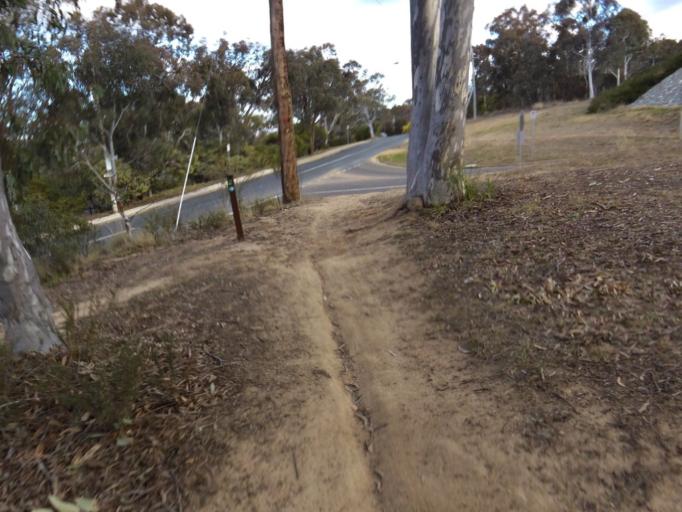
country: AU
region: Australian Capital Territory
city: Acton
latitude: -35.2651
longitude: 149.1114
